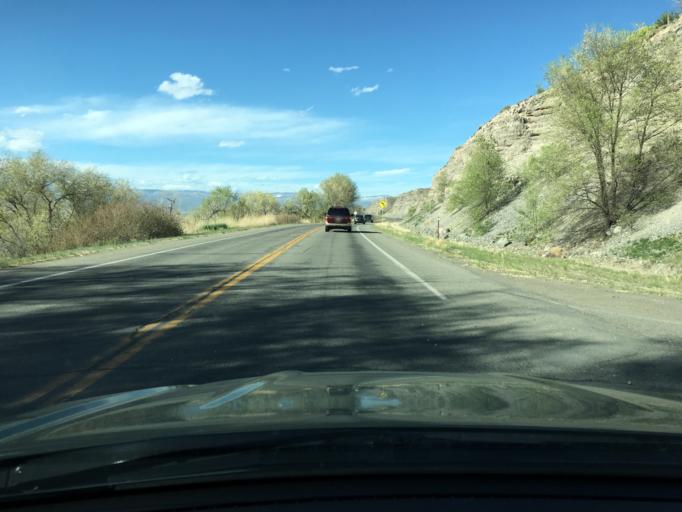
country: US
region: Colorado
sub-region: Delta County
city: Orchard City
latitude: 38.7772
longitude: -108.0000
